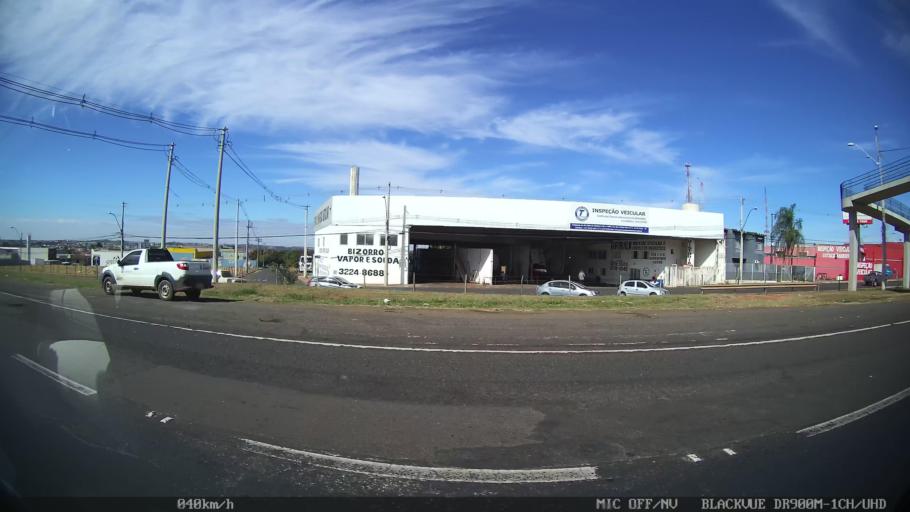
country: BR
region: Sao Paulo
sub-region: Sao Jose Do Rio Preto
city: Sao Jose do Rio Preto
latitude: -20.8278
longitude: -49.3588
